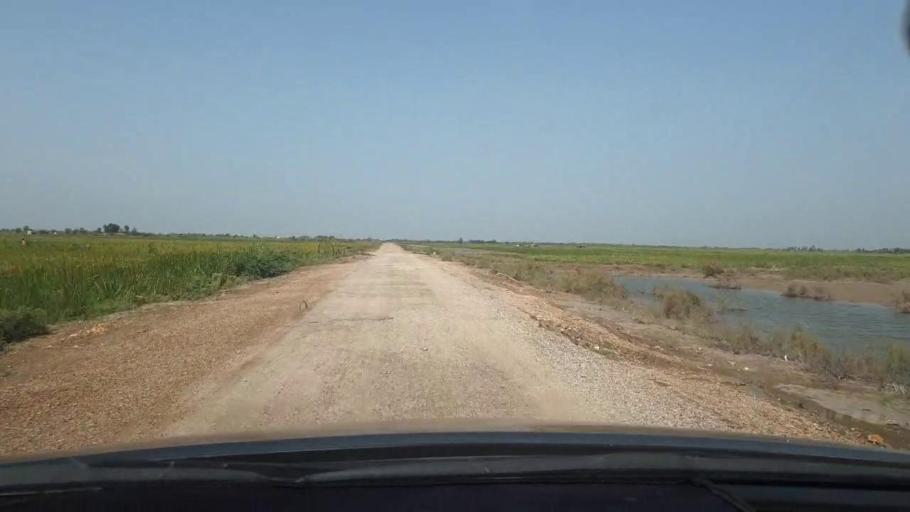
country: PK
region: Sindh
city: Tando Bago
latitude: 24.7179
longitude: 69.1169
